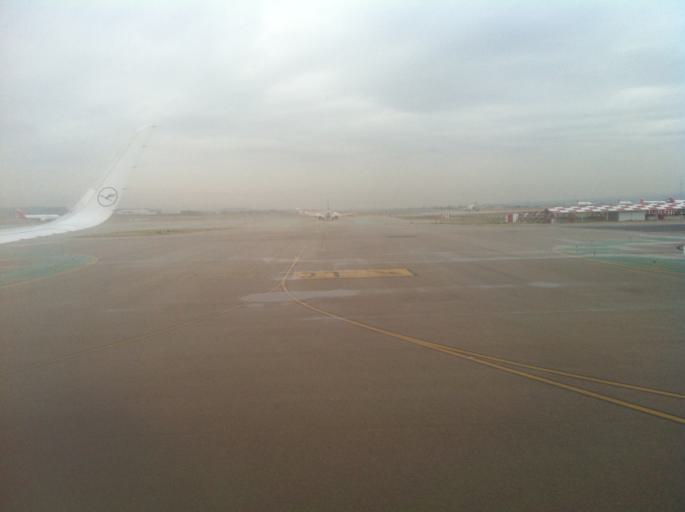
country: ES
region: Madrid
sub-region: Provincia de Madrid
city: Barajas de Madrid
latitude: 40.4877
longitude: -3.5761
